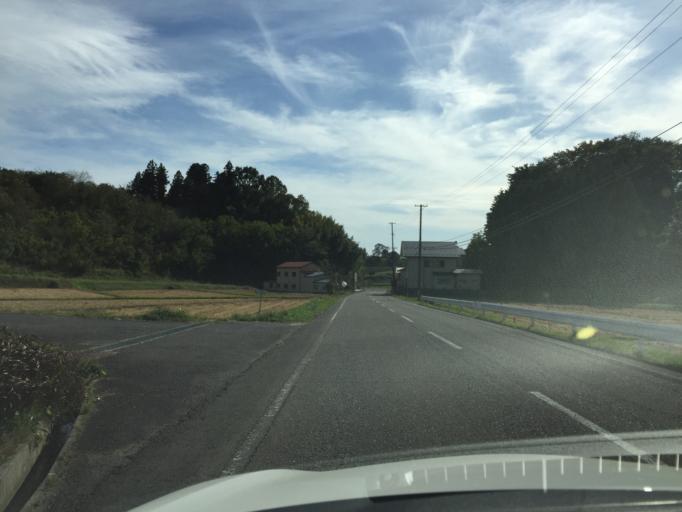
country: JP
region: Fukushima
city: Miharu
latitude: 37.4709
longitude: 140.4929
